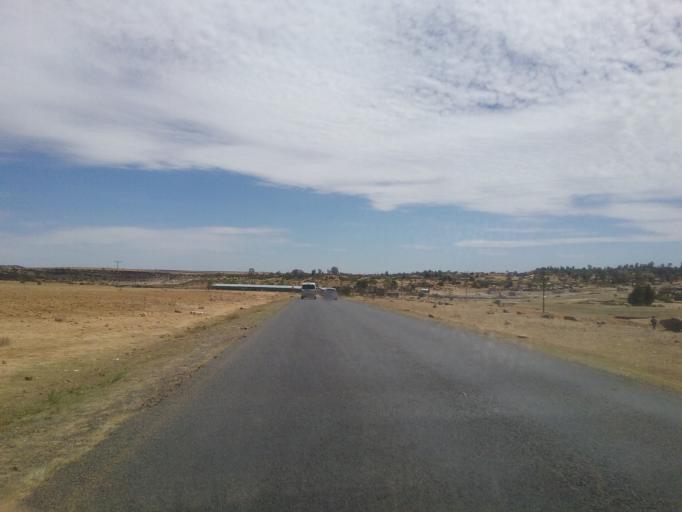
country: LS
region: Mafeteng
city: Mafeteng
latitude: -29.8500
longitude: 27.2302
